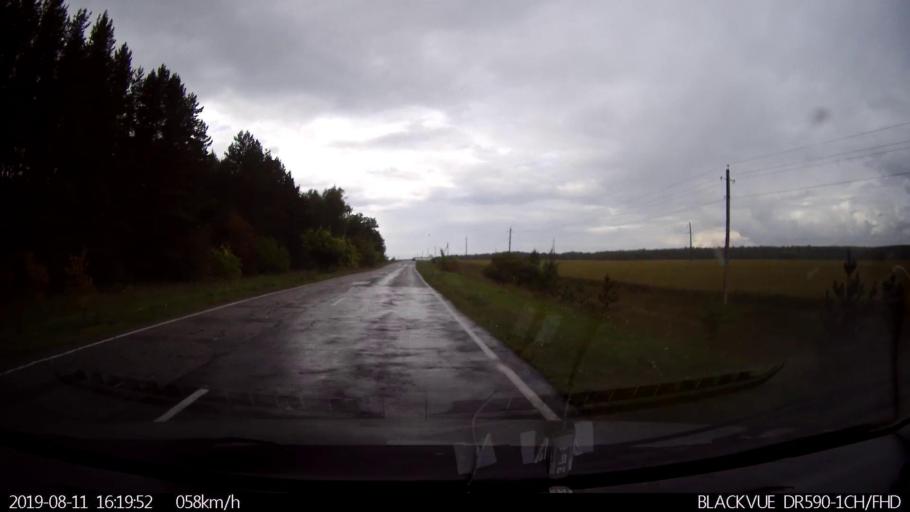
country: RU
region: Ulyanovsk
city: Mayna
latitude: 54.0674
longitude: 47.6054
